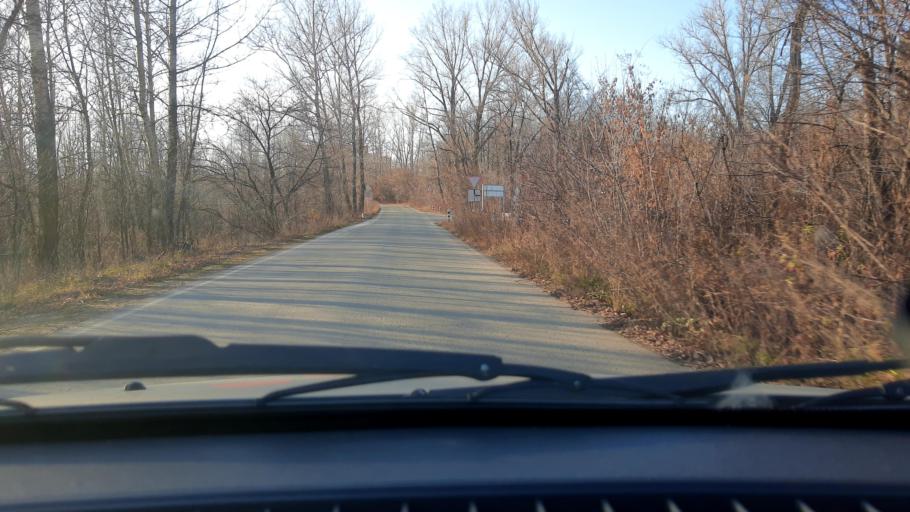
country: RU
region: Bashkortostan
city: Ufa
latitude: 54.6655
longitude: 55.9603
